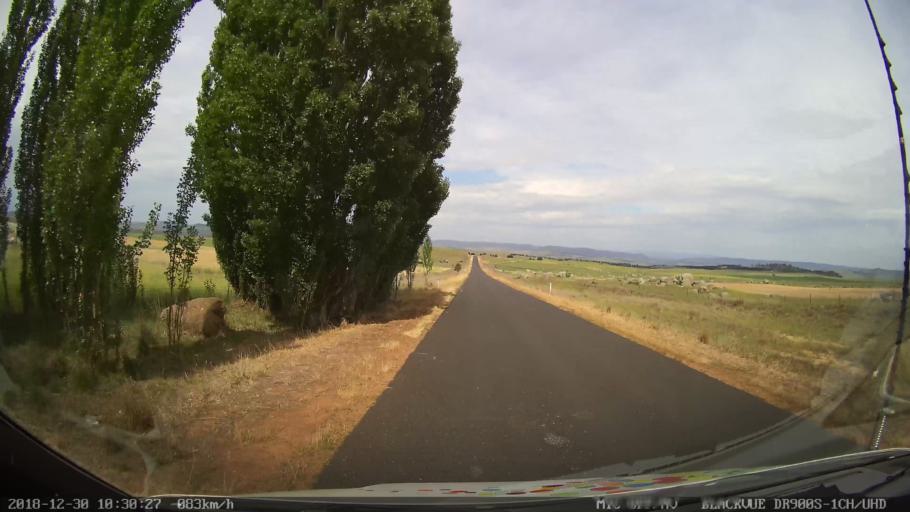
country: AU
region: New South Wales
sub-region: Snowy River
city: Berridale
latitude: -36.5038
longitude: 148.8948
